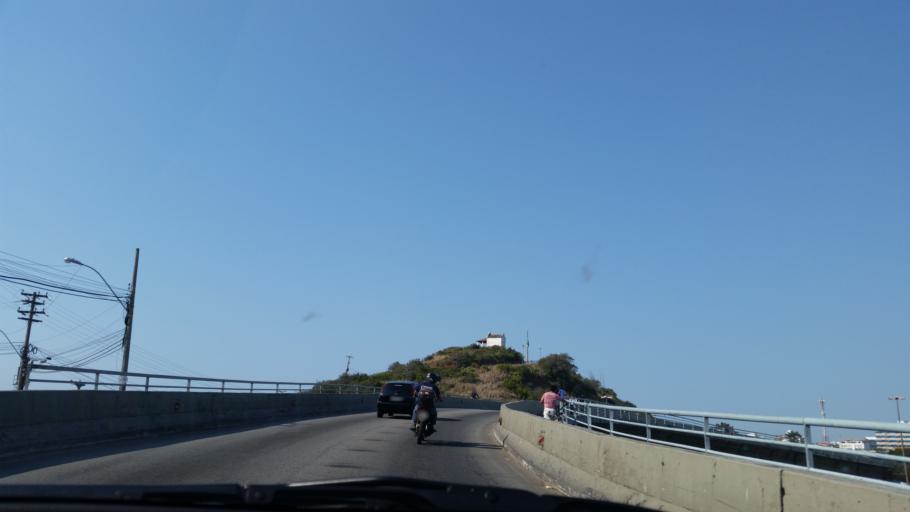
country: BR
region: Rio de Janeiro
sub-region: Cabo Frio
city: Cabo Frio
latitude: -22.8764
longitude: -42.0225
